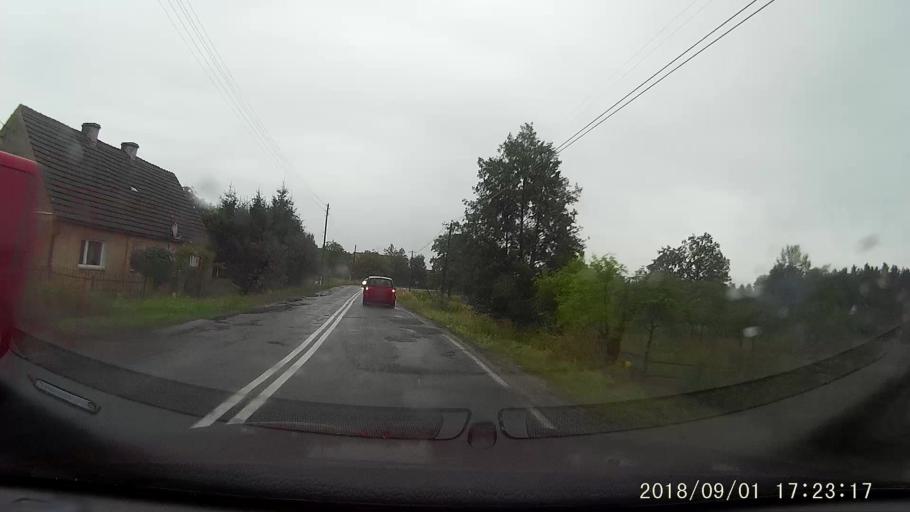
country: PL
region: Lubusz
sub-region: Powiat zaganski
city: Zagan
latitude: 51.7006
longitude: 15.2965
